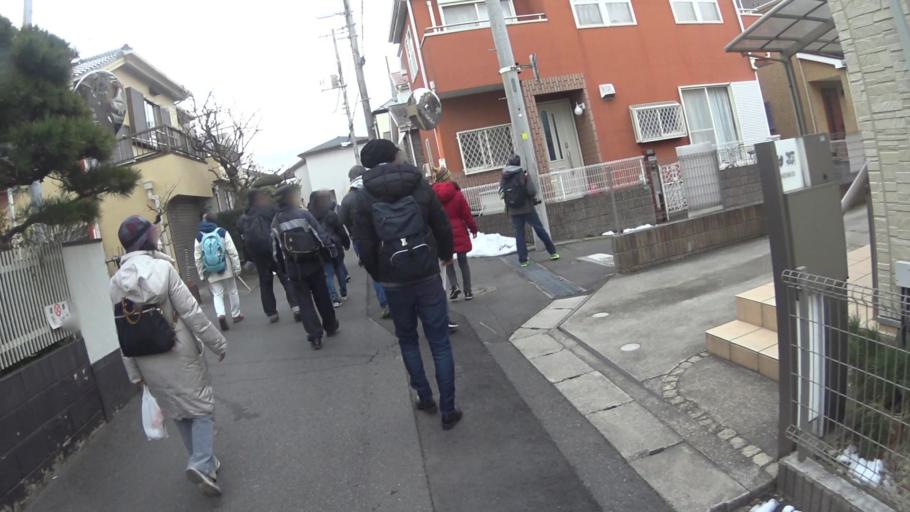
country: JP
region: Chiba
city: Funabashi
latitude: 35.7466
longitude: 139.9924
